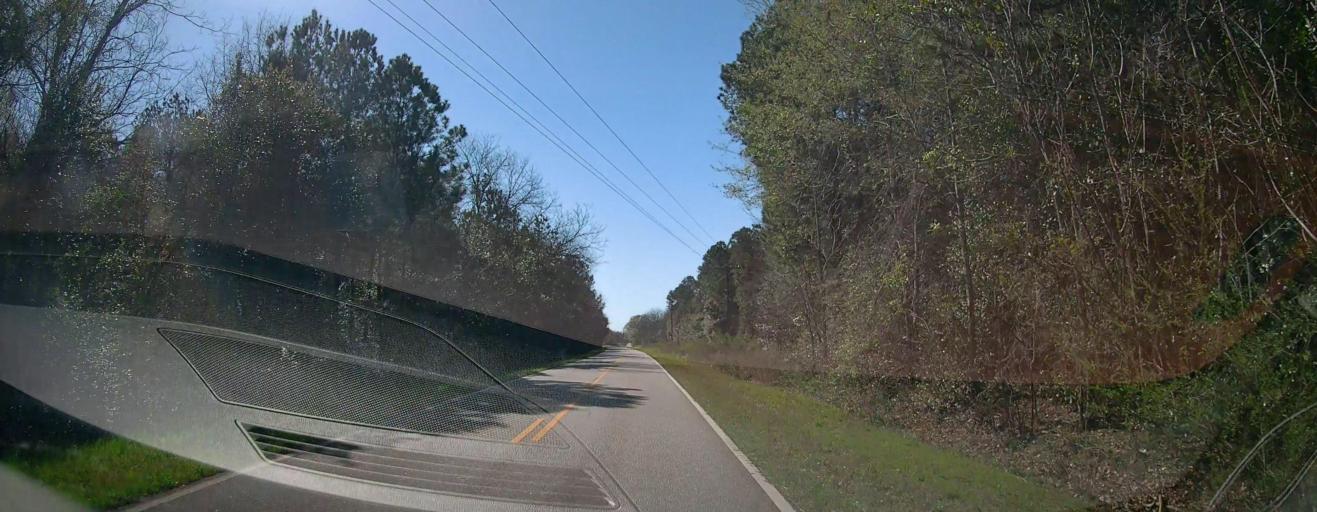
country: US
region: Georgia
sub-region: Peach County
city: Byron
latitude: 32.6444
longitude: -83.8204
